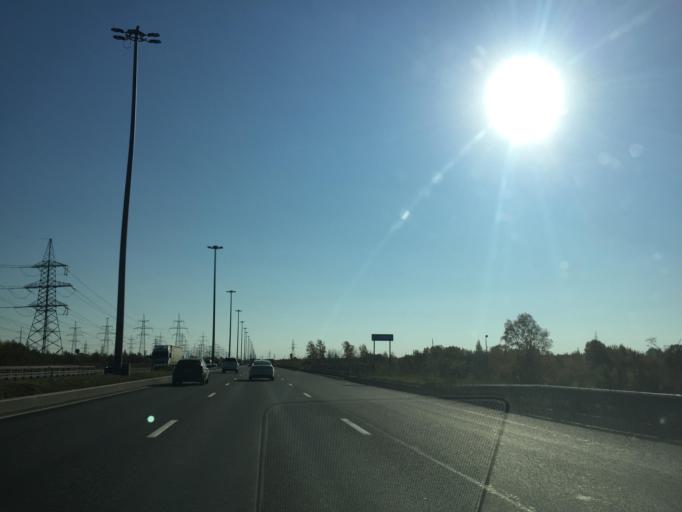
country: RU
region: St.-Petersburg
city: Petro-Slavyanka
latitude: 59.7637
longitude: 30.5063
